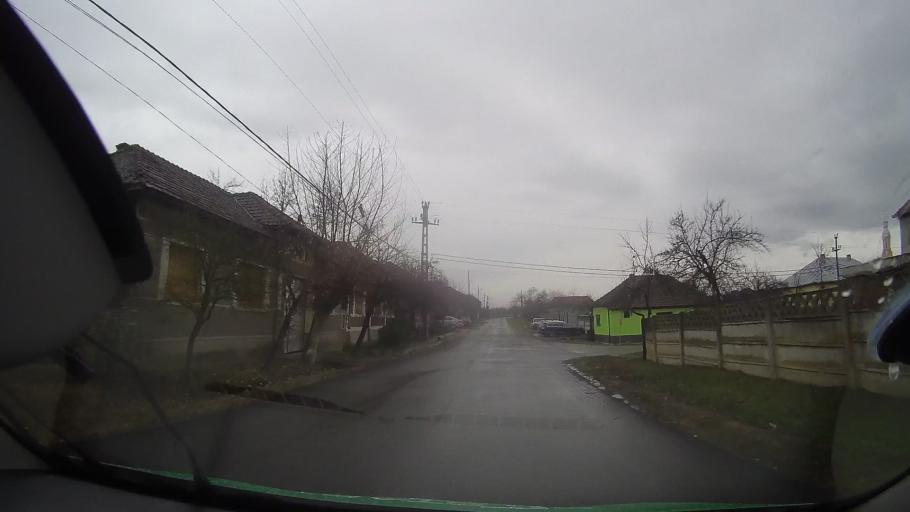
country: RO
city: Capalna
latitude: 46.7363
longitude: 22.1027
